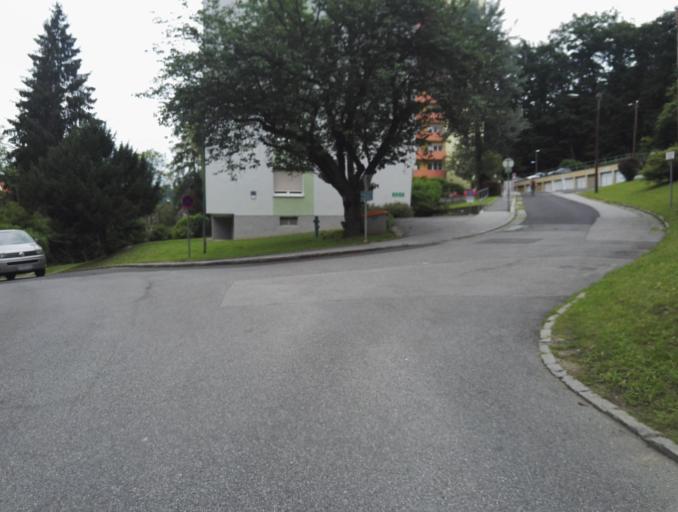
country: AT
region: Styria
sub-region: Graz Stadt
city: Graz
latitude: 47.0820
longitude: 15.4724
